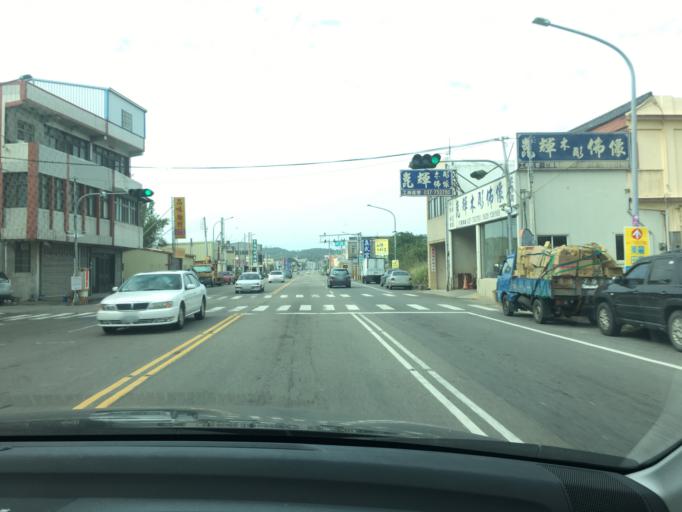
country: TW
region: Taiwan
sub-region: Miaoli
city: Miaoli
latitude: 24.4964
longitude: 120.6999
